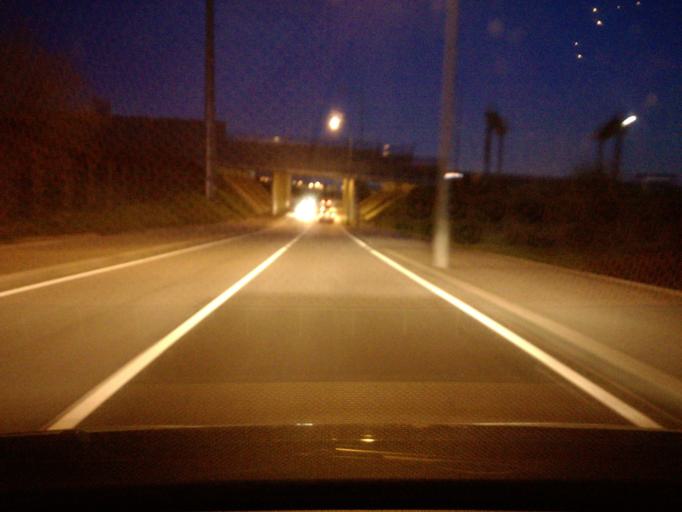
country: PT
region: Porto
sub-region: Maia
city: Maia
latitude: 41.2403
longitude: -8.6375
